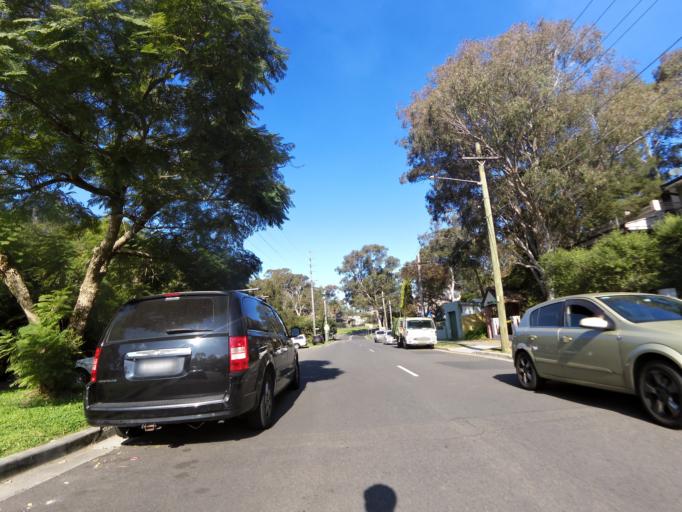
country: AU
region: New South Wales
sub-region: Sutherland Shire
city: Como
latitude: -34.0007
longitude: 151.0678
